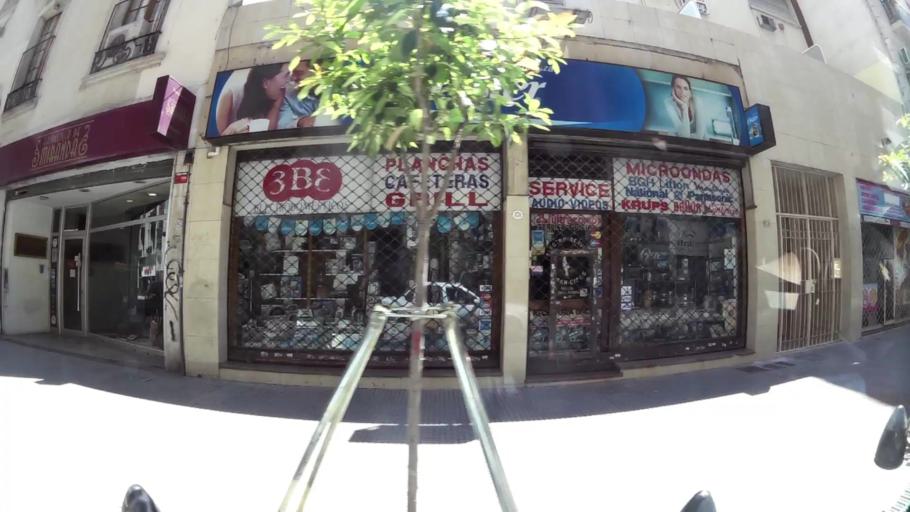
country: AR
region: Buenos Aires F.D.
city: Buenos Aires
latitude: -34.5980
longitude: -58.3782
